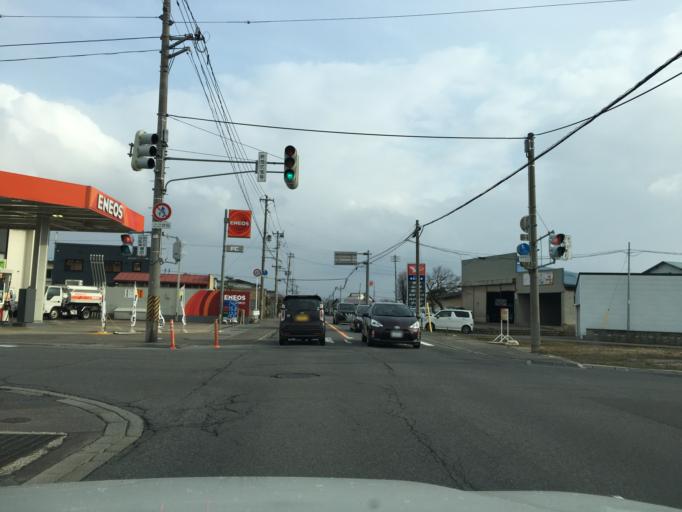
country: JP
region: Aomori
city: Namioka
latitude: 40.7088
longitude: 140.5906
